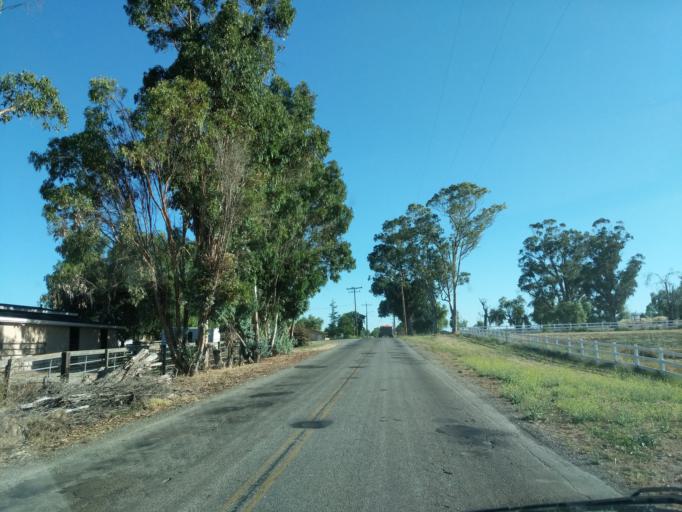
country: US
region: California
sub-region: San Benito County
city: Ridgemark
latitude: 36.8192
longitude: -121.3455
